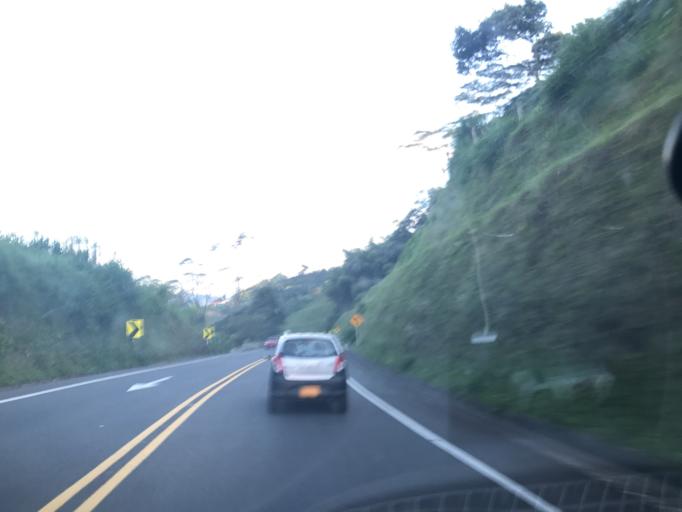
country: CO
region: Risaralda
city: Pereira
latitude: 4.7759
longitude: -75.7137
